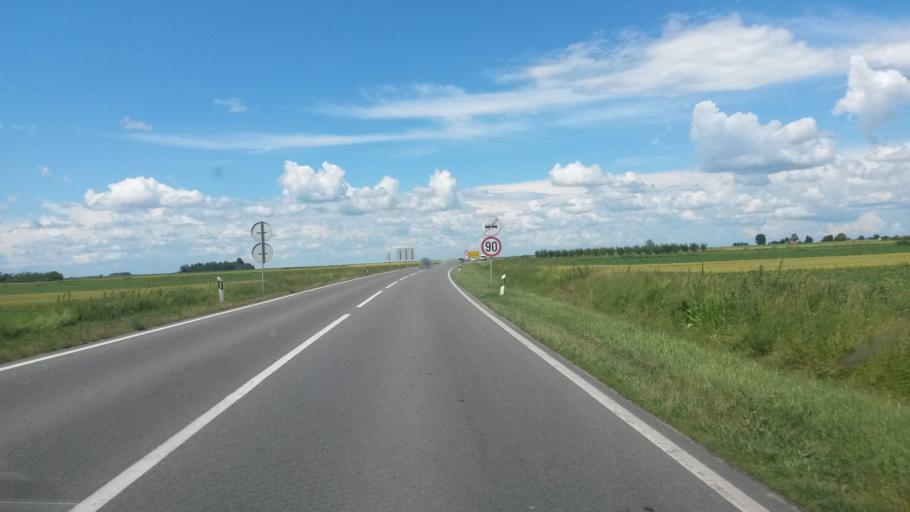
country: HR
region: Osjecko-Baranjska
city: Cepin
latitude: 45.5175
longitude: 18.5369
